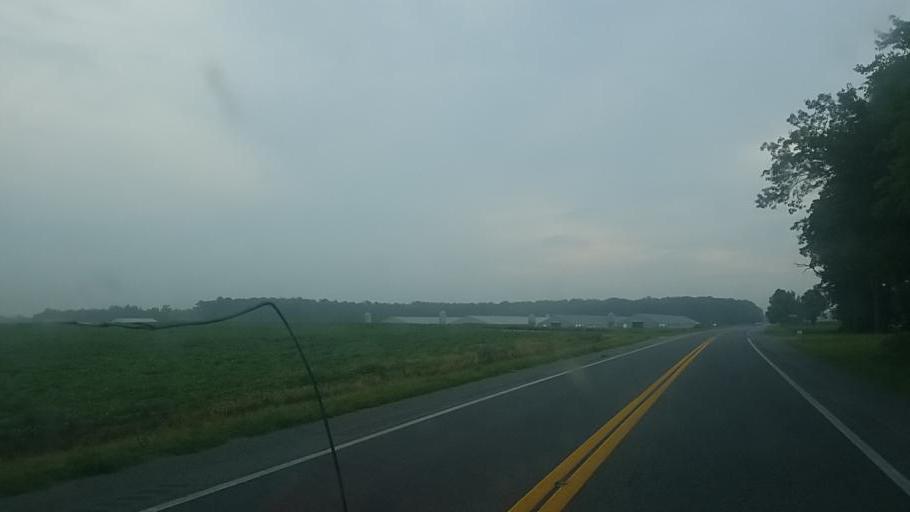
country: US
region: Maryland
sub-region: Wicomico County
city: Pittsville
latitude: 38.4523
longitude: -75.4097
